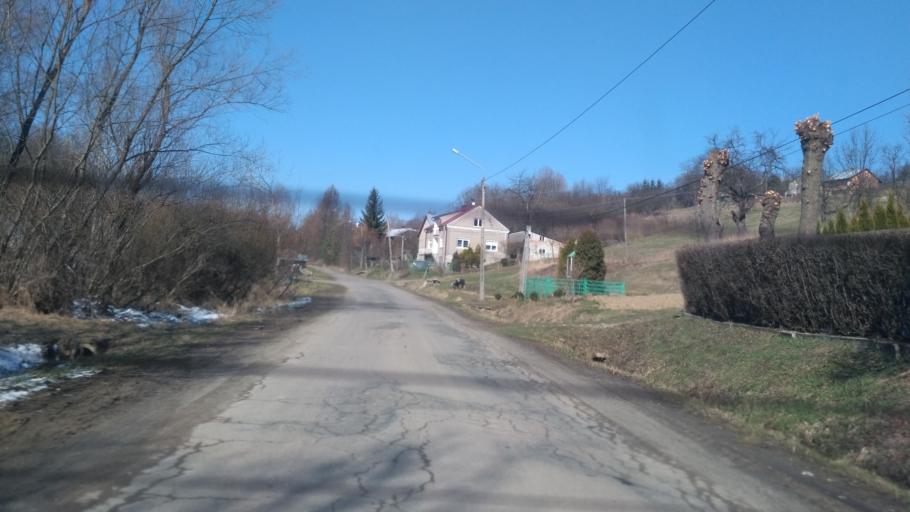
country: PL
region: Subcarpathian Voivodeship
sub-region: Powiat strzyzowski
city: Gwoznica Gorna
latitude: 49.8169
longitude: 22.0244
